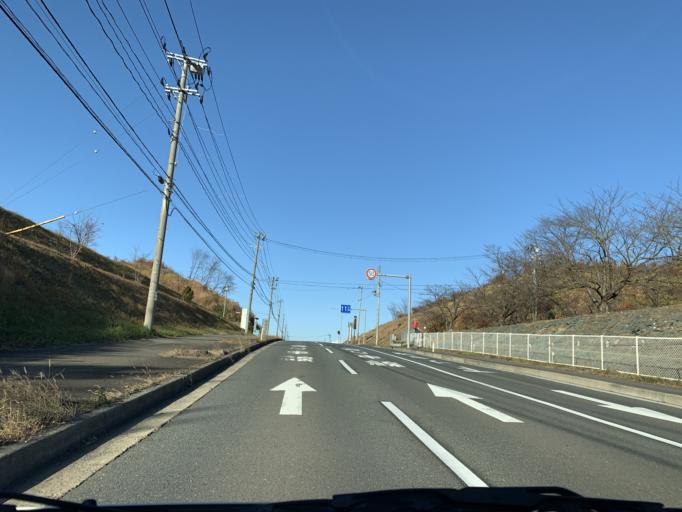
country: JP
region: Iwate
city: Mizusawa
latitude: 39.2037
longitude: 141.1776
